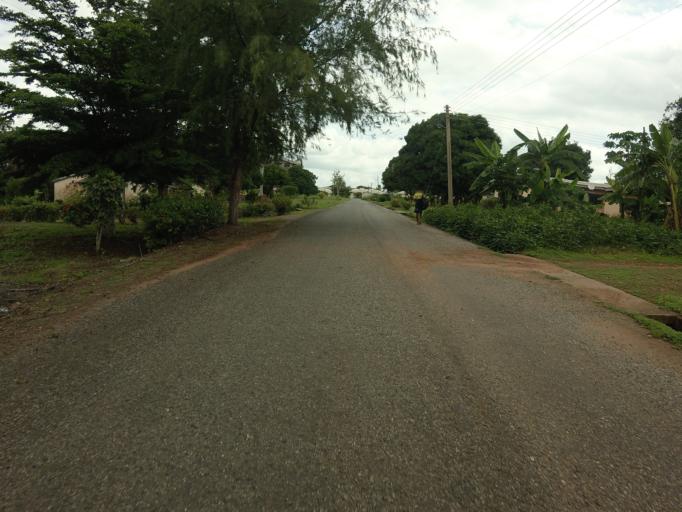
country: GH
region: Volta
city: Ho
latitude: 6.5914
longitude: 0.4664
